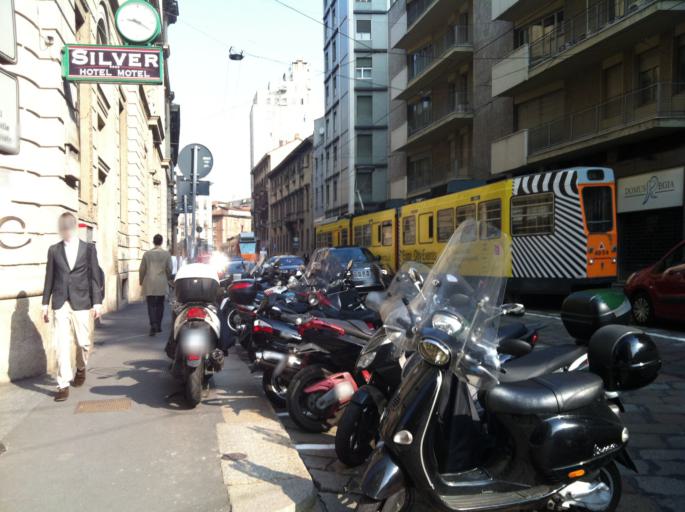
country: IT
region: Lombardy
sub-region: Citta metropolitana di Milano
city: Milano
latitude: 45.4594
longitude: 9.1904
